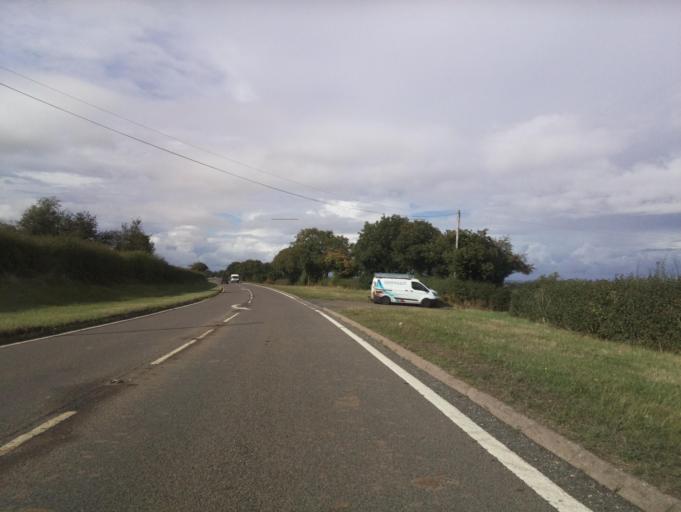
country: GB
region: England
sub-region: Shropshire
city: Bridgnorth
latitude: 52.5817
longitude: -2.3951
